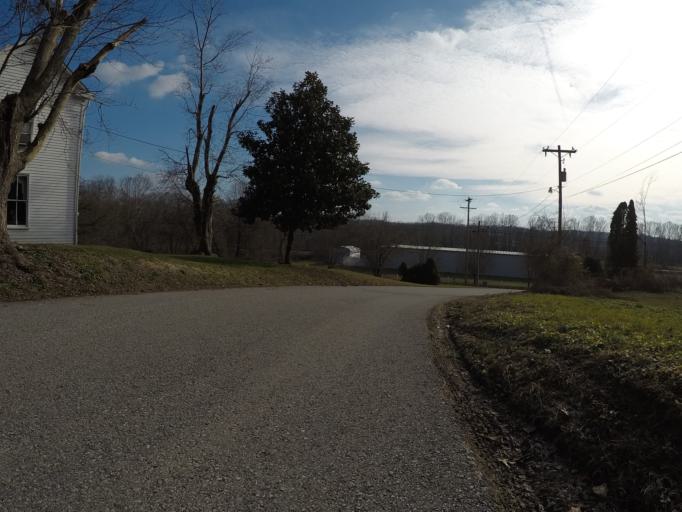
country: US
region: West Virginia
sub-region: Cabell County
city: Pea Ridge
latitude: 38.4227
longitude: -82.3421
